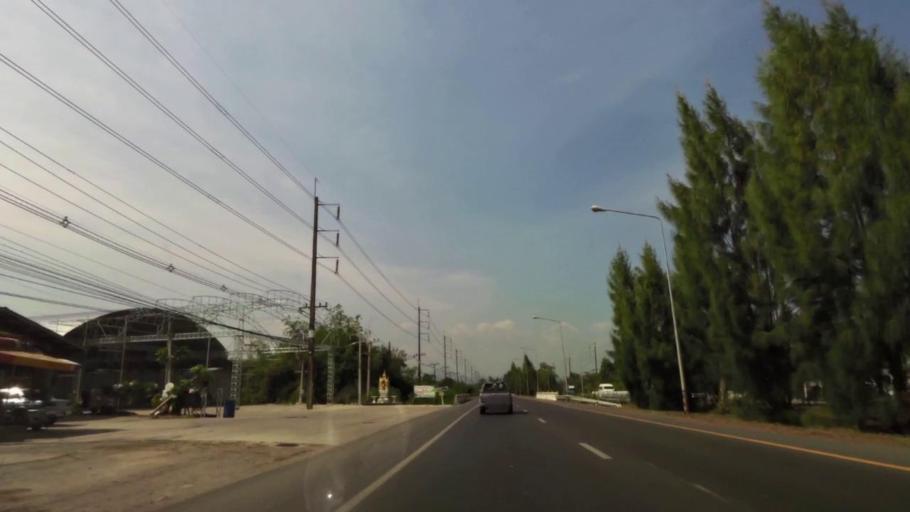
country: TH
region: Chanthaburi
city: Chanthaburi
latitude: 12.6389
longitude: 102.1351
